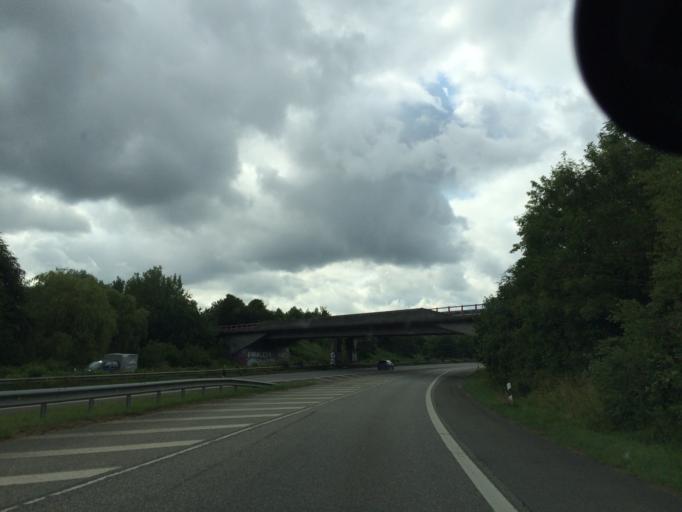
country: DE
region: Schleswig-Holstein
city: Kiel
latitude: 54.3488
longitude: 10.1198
